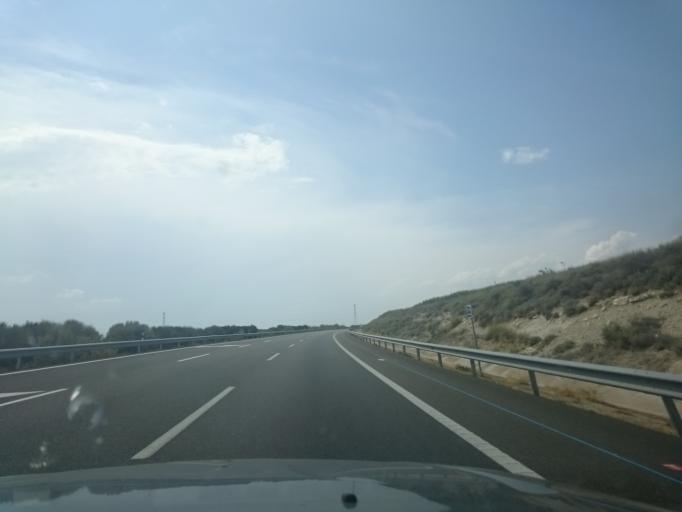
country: ES
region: Aragon
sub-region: Provincia de Huesca
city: Penalba
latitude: 41.5130
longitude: -0.0723
